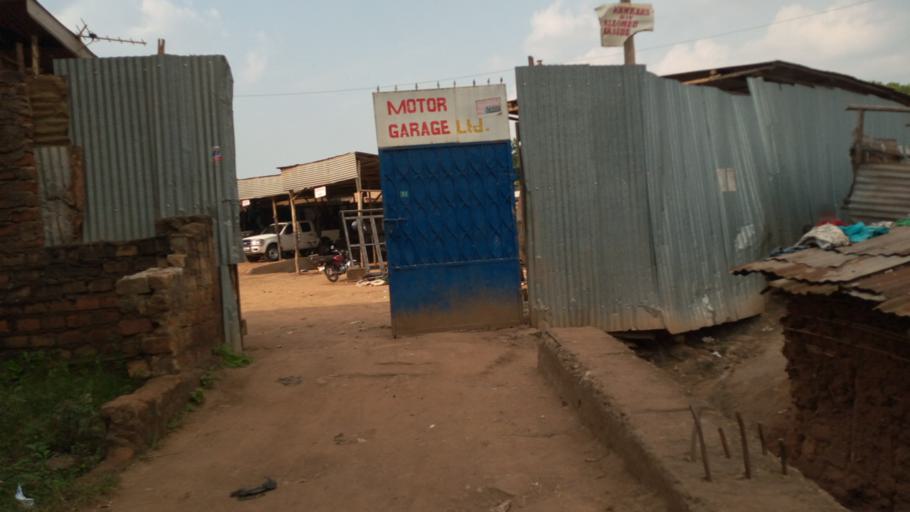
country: UG
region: Central Region
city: Kampala Central Division
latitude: 0.3244
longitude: 32.5672
